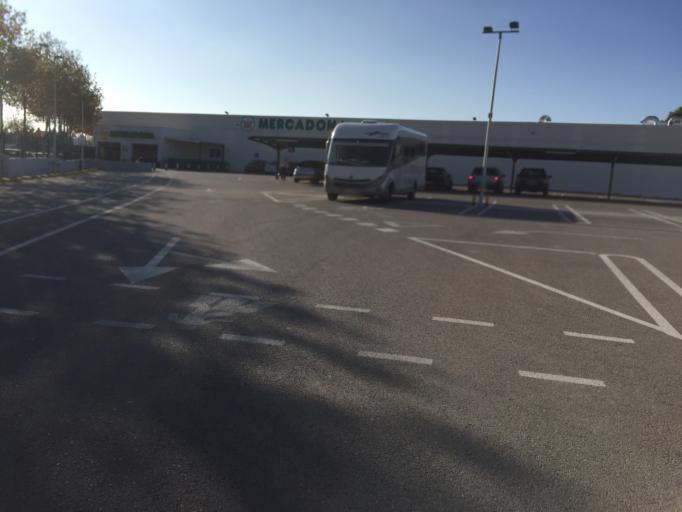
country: ES
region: Andalusia
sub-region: Provincia de Cadiz
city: Conil de la Frontera
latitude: 36.2845
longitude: -6.0878
